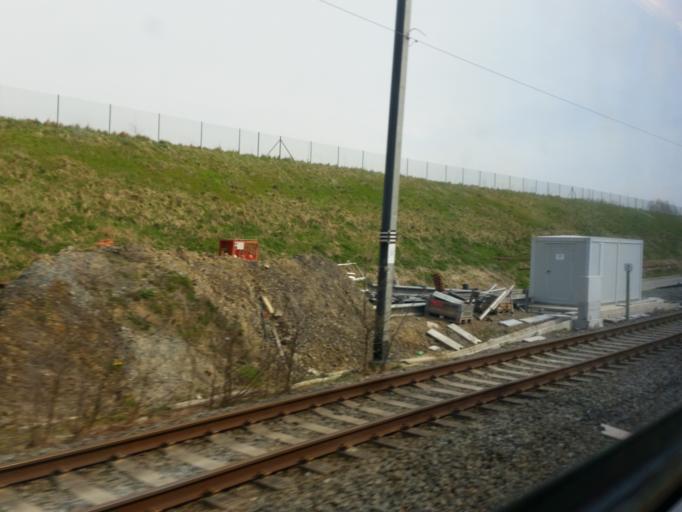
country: BE
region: Flanders
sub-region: Provincie Vlaams-Brabant
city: Ternat
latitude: 50.8727
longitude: 4.1327
